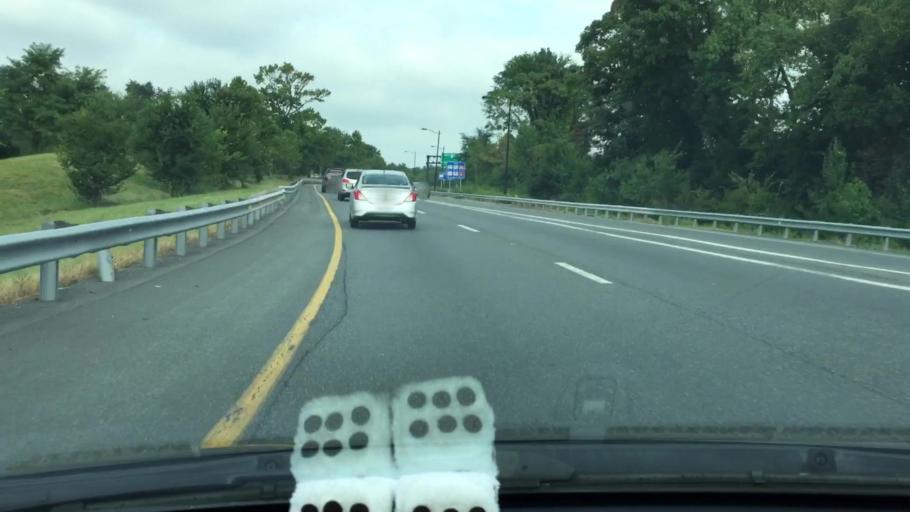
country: US
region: Delaware
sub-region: New Castle County
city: Wilmington
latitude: 39.7694
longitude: -75.5414
